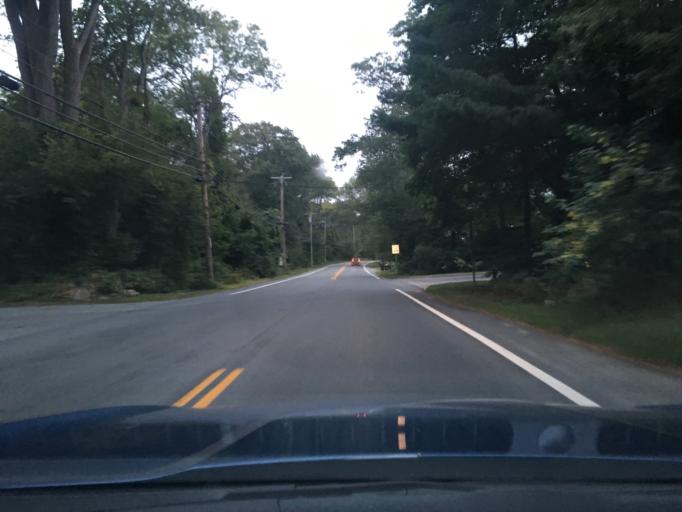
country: US
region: Rhode Island
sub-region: Kent County
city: West Warwick
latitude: 41.6622
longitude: -71.5080
